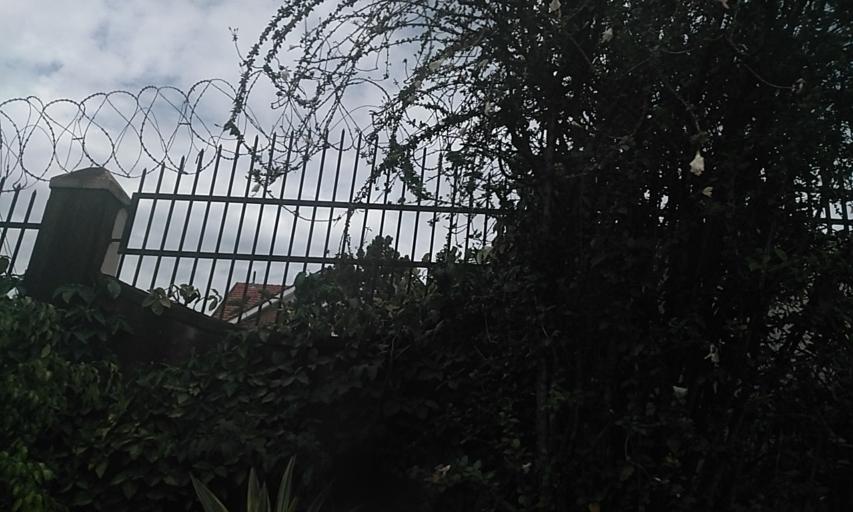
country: UG
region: Central Region
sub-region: Kampala District
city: Kampala
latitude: 0.3248
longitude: 32.5934
